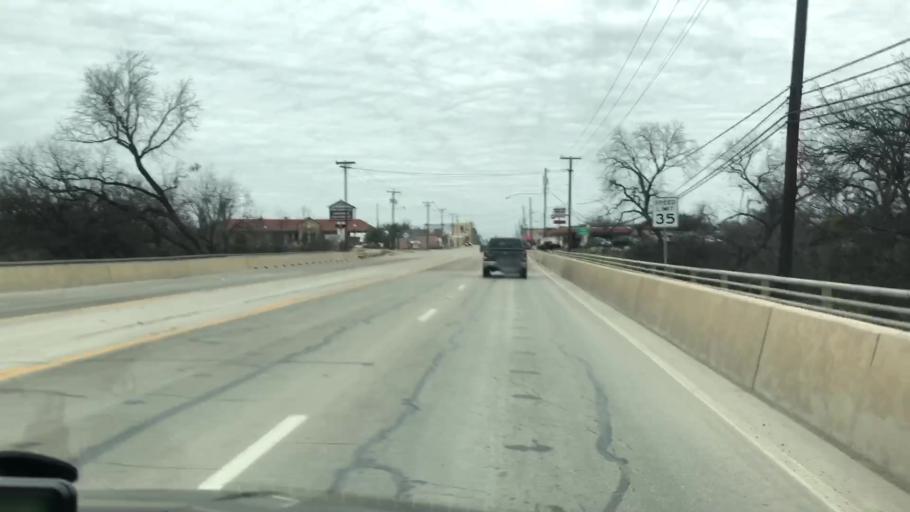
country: US
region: Texas
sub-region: Jack County
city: Jacksboro
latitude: 33.2136
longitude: -98.1588
